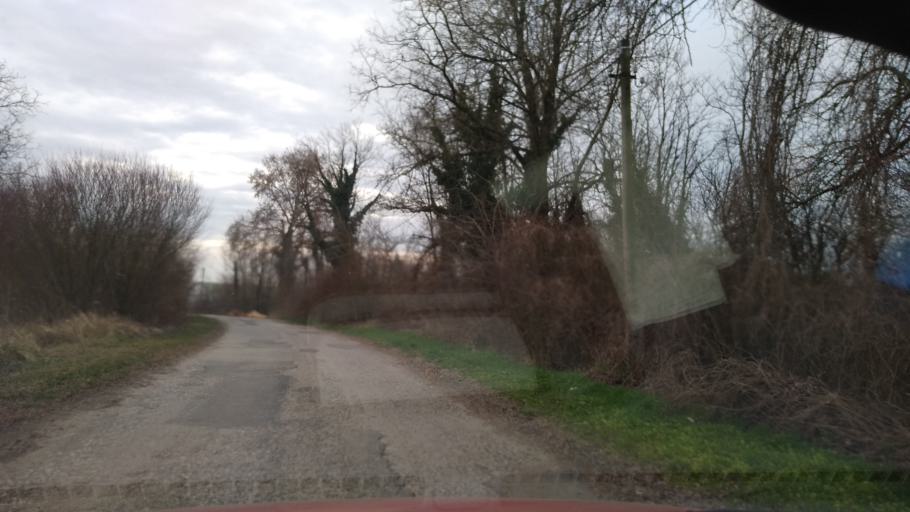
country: HU
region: Somogy
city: Barcs
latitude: 45.9512
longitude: 17.4276
